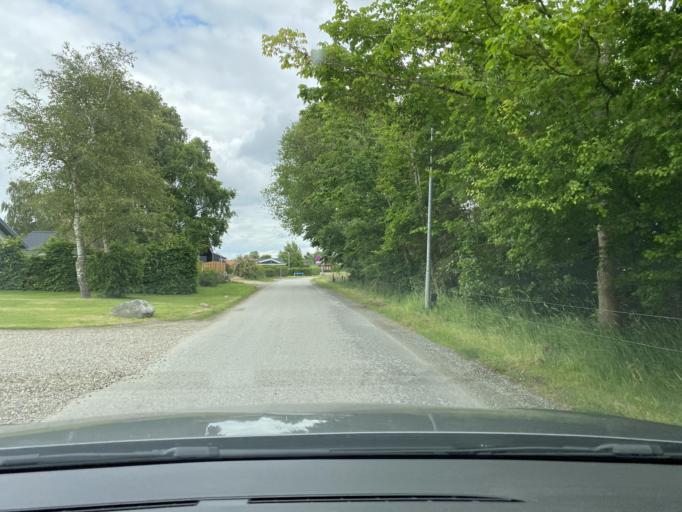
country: DK
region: South Denmark
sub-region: Vejle Kommune
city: Brejning
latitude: 55.6349
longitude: 9.7382
